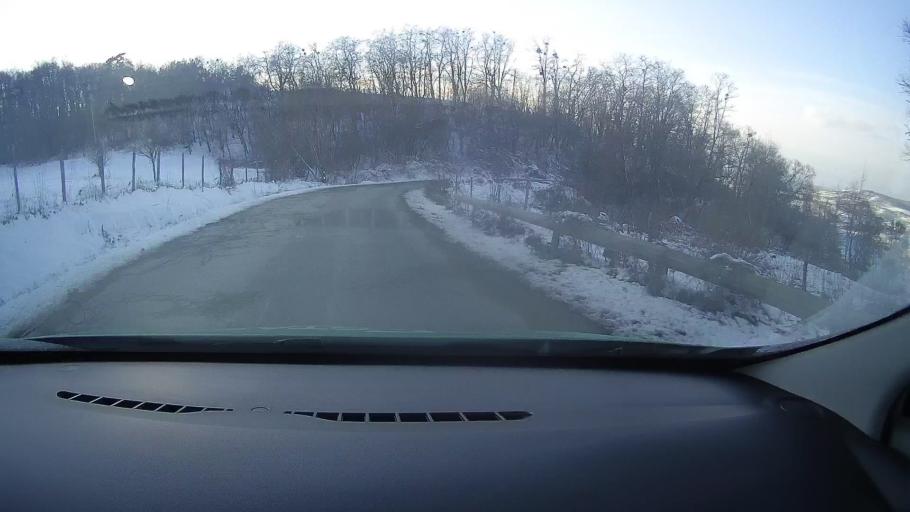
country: RO
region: Sibiu
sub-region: Oras Agnita
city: Ruja
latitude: 45.9865
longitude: 24.6816
